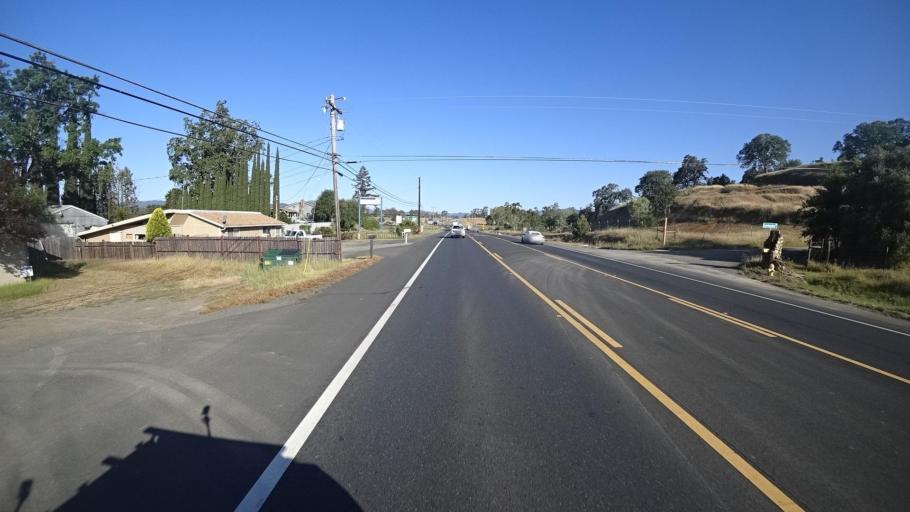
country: US
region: California
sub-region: Lake County
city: Nice
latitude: 39.1285
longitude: -122.8673
